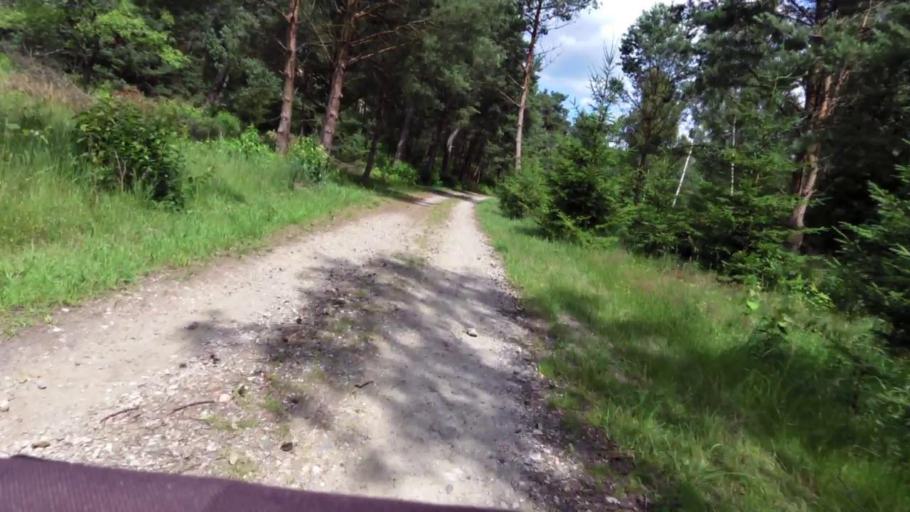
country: PL
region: West Pomeranian Voivodeship
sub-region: Powiat gryficki
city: Mrzezyno
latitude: 54.1270
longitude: 15.2472
